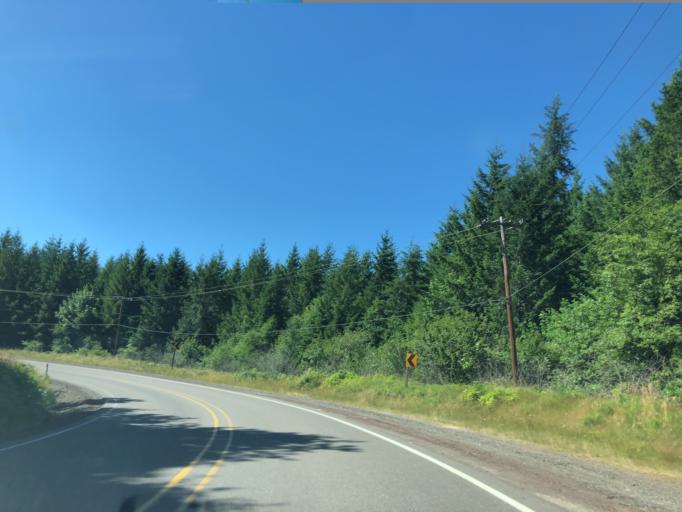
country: US
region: Oregon
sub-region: Linn County
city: Sweet Home
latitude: 44.4054
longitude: -122.5671
